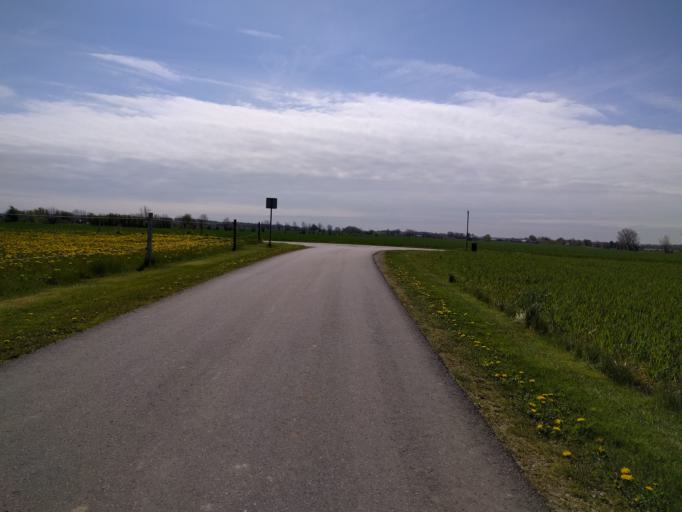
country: DK
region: South Denmark
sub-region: Kerteminde Kommune
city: Munkebo
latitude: 55.4454
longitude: 10.5968
